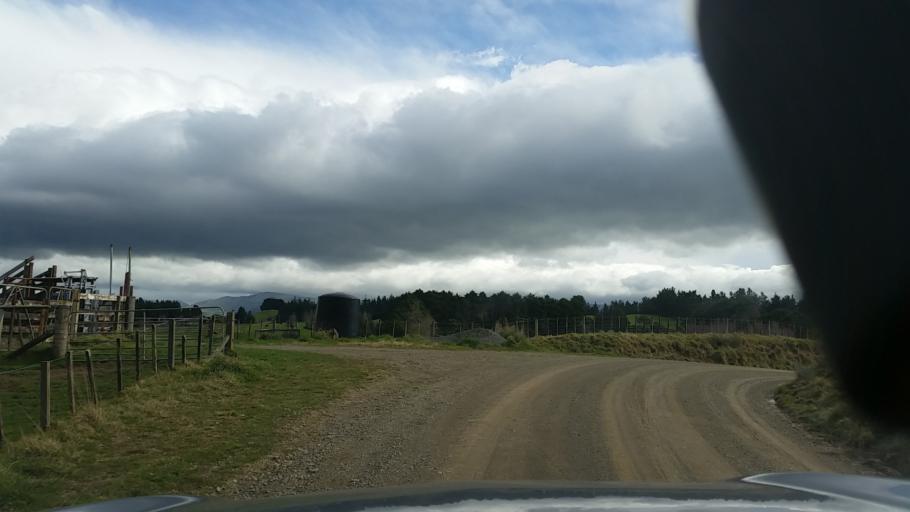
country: NZ
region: Hawke's Bay
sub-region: Napier City
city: Napier
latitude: -39.2064
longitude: 176.9318
